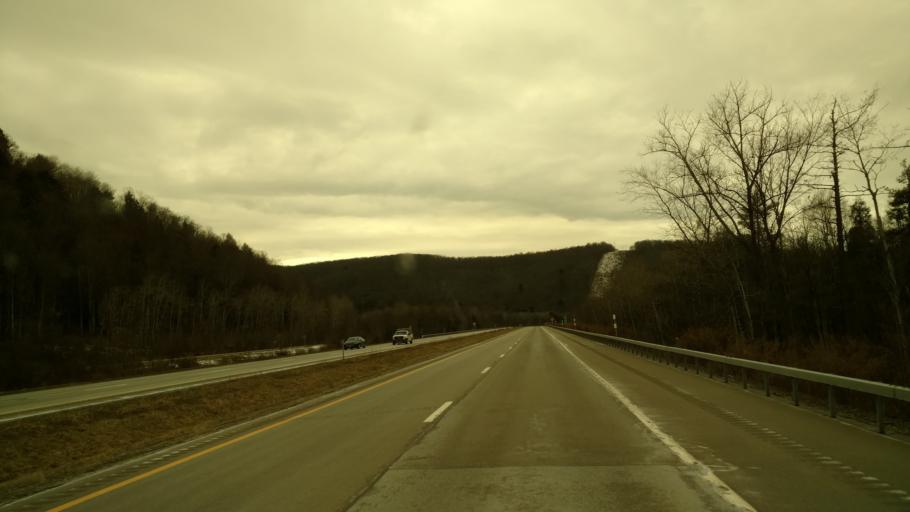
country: US
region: New York
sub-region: Cattaraugus County
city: Salamanca
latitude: 42.1028
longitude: -78.7994
